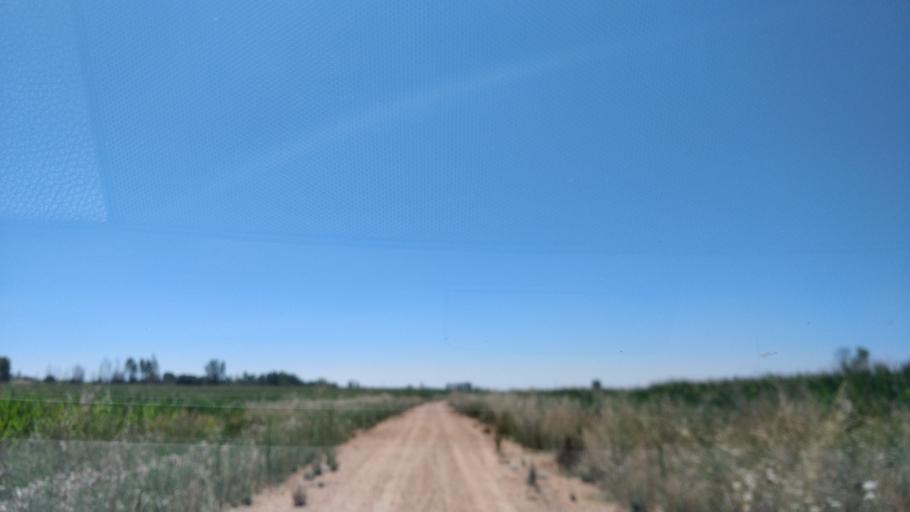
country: ES
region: Castille and Leon
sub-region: Provincia de Leon
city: Bustillo del Paramo
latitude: 42.4779
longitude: -5.8082
